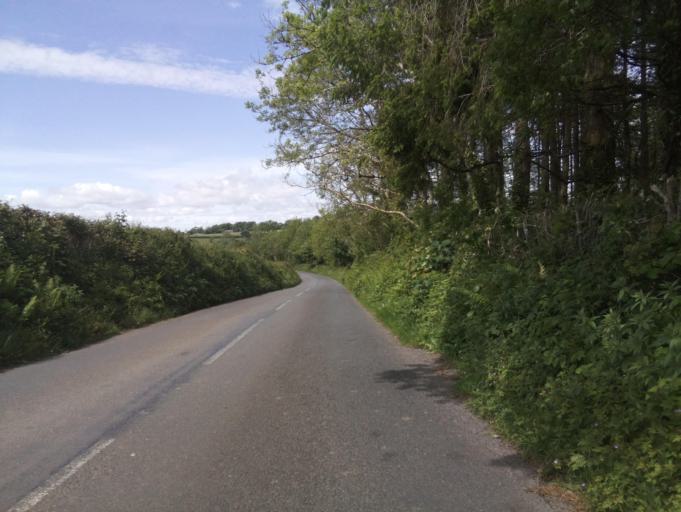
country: GB
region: England
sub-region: Devon
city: Kingsbridge
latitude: 50.3629
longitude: -3.7689
